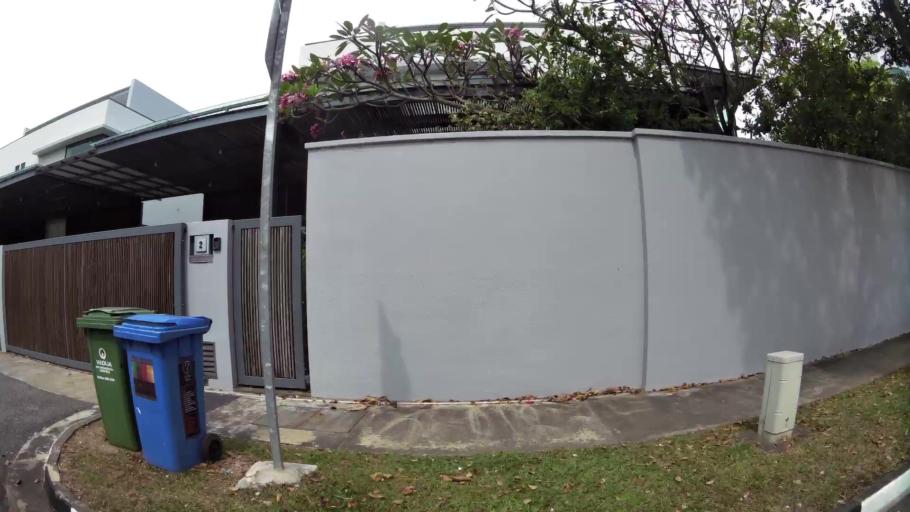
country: SG
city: Singapore
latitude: 1.3218
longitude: 103.8102
